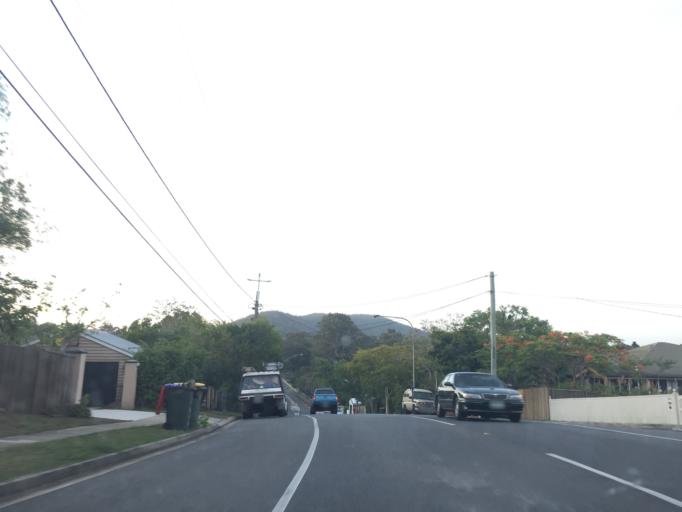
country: AU
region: Queensland
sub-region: Brisbane
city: Milton
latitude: -27.4535
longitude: 152.9810
